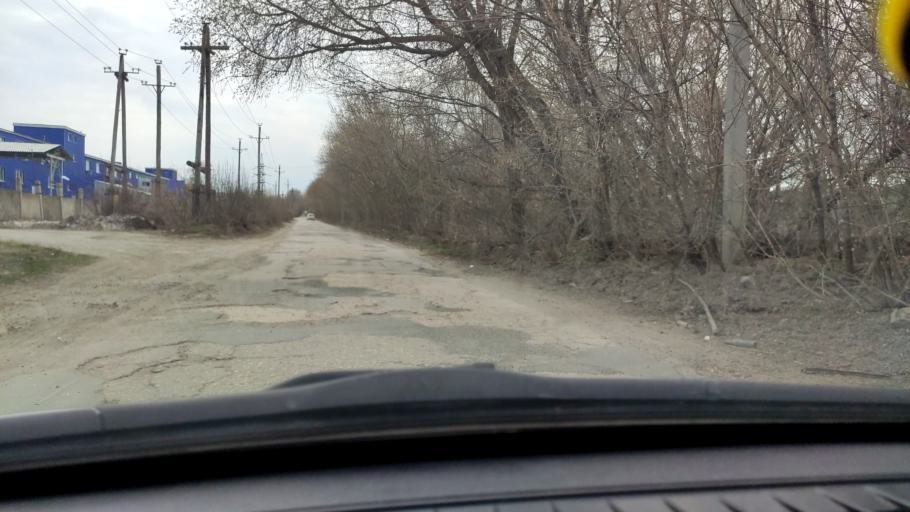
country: RU
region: Samara
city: Tol'yatti
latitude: 53.5238
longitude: 49.4561
